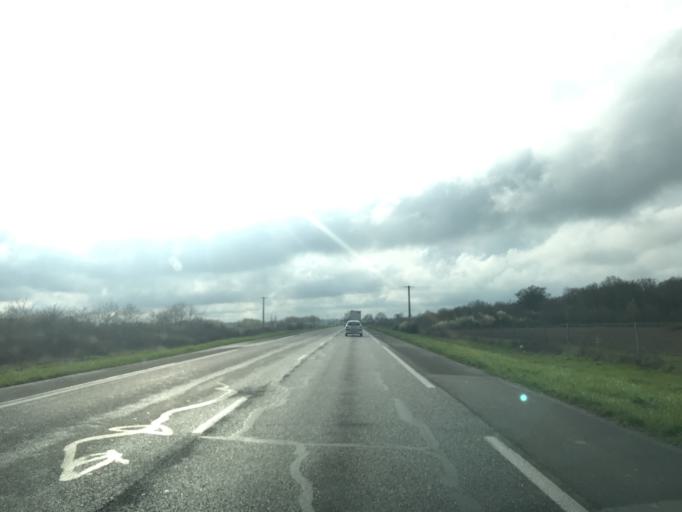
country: FR
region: Centre
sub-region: Departement du Loiret
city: Nevoy
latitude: 47.7134
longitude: 2.5985
